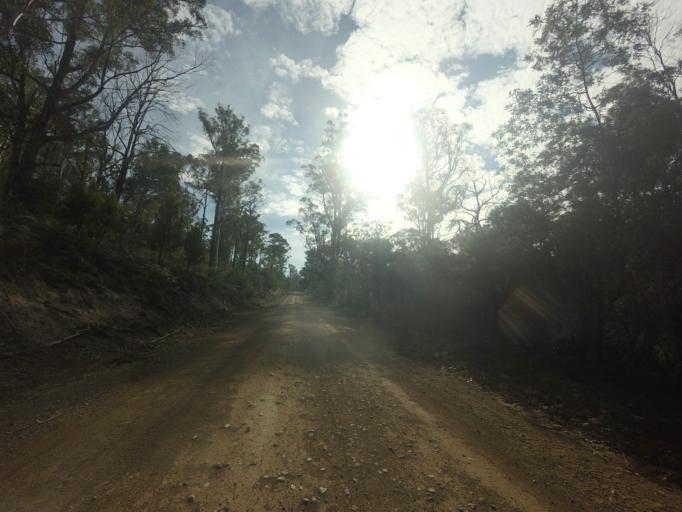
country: AU
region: Tasmania
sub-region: Sorell
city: Sorell
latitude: -42.5629
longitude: 147.4670
